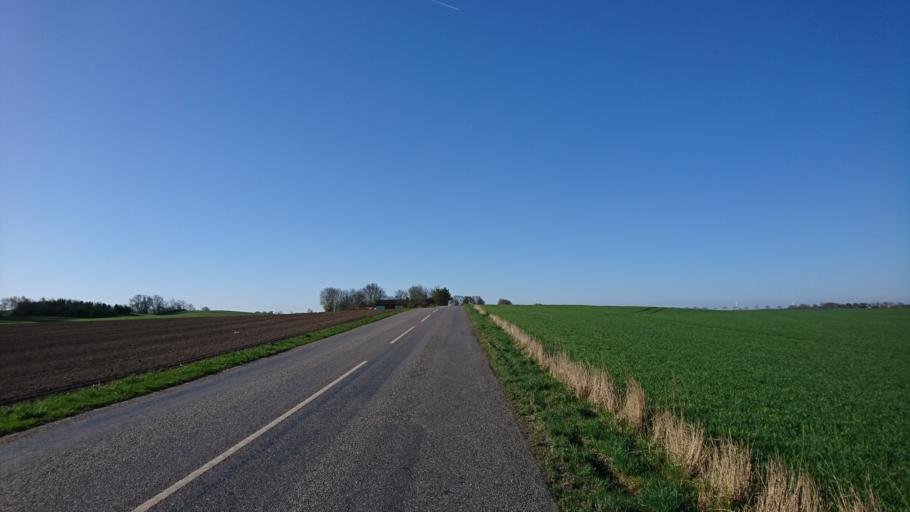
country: DK
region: Capital Region
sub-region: Frederikssund Kommune
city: Skibby
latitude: 55.7351
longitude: 11.9290
